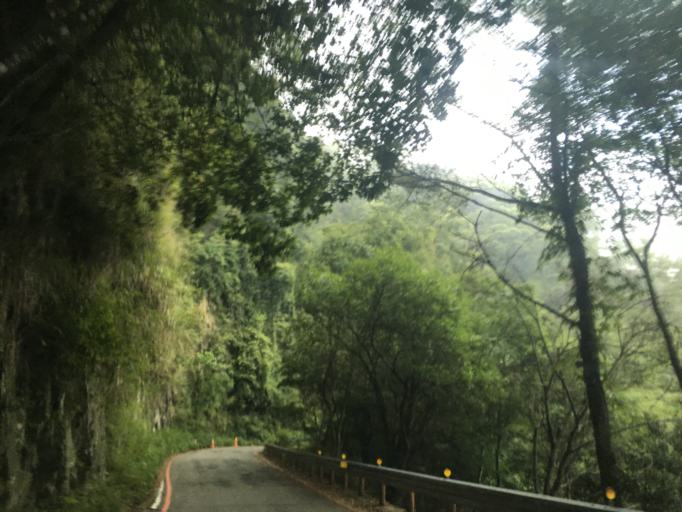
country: TW
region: Taiwan
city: Fengyuan
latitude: 24.2334
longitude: 120.9600
